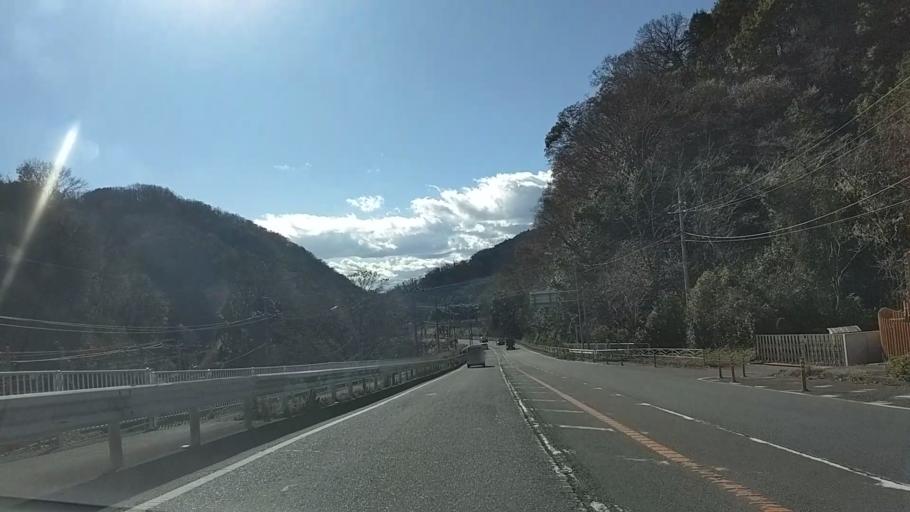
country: JP
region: Kanagawa
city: Hadano
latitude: 35.3708
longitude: 139.1630
